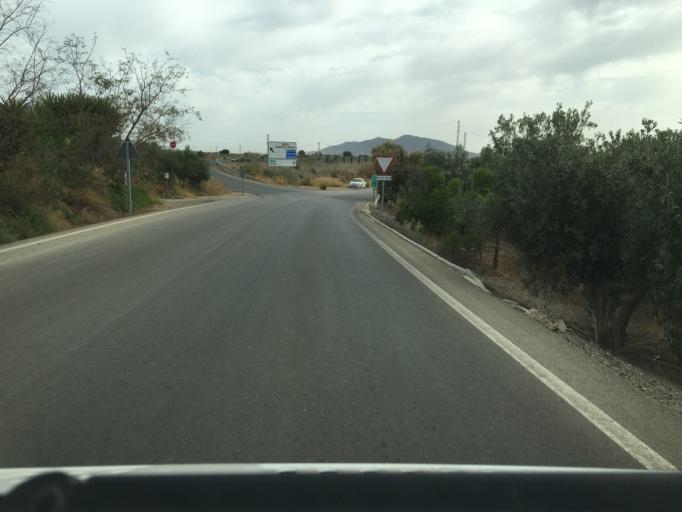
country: ES
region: Andalusia
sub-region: Provincia de Almeria
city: Huercal-Overa
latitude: 37.4122
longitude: -1.9148
